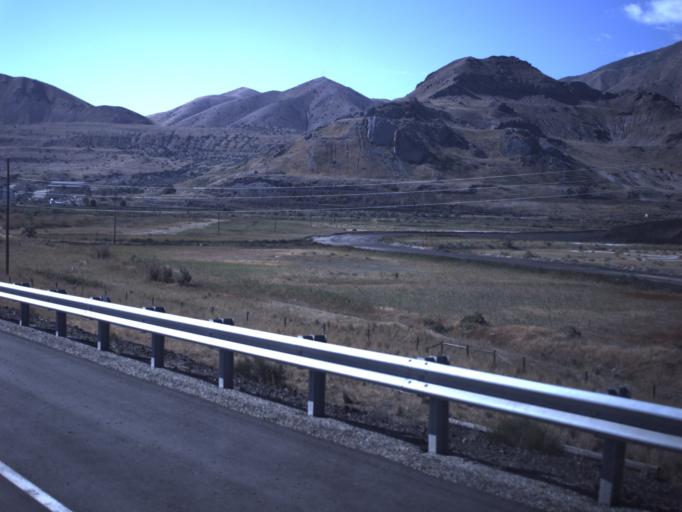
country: US
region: Utah
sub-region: Salt Lake County
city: Magna
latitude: 40.7404
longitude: -112.1772
